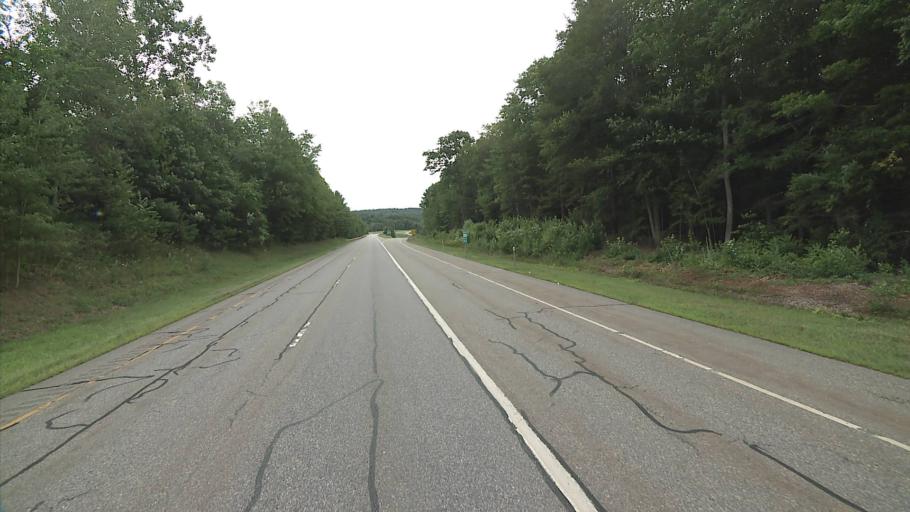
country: US
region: Connecticut
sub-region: Litchfield County
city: Winsted
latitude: 41.8837
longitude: -73.0715
